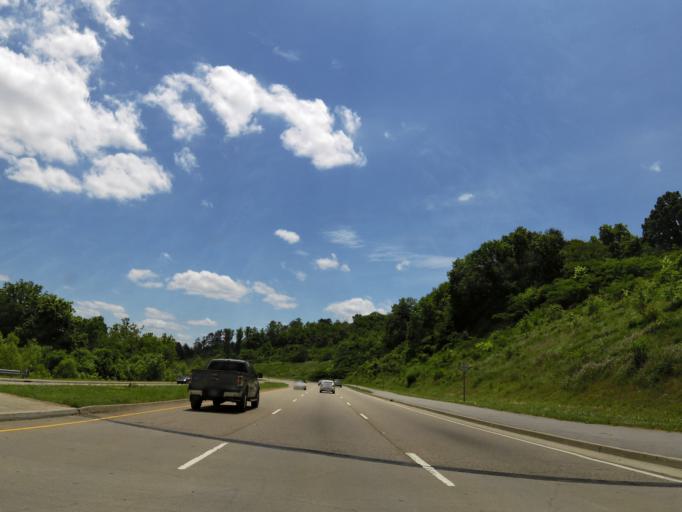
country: US
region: Tennessee
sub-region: Sevier County
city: Sevierville
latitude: 35.8572
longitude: -83.5449
